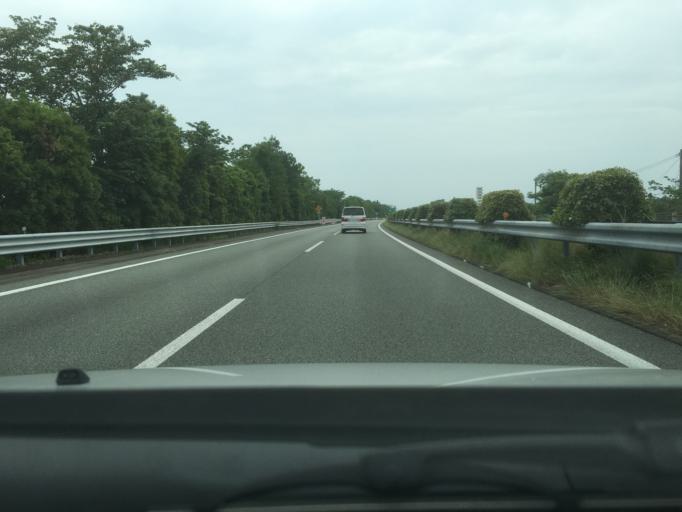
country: JP
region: Kumamoto
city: Ozu
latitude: 32.8047
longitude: 130.7932
